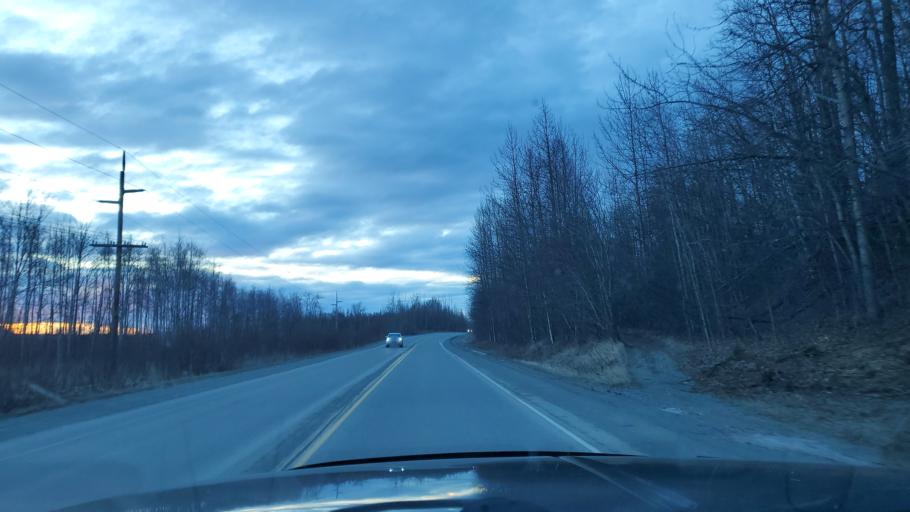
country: US
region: Alaska
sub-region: Matanuska-Susitna Borough
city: Lakes
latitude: 61.6067
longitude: -149.3403
